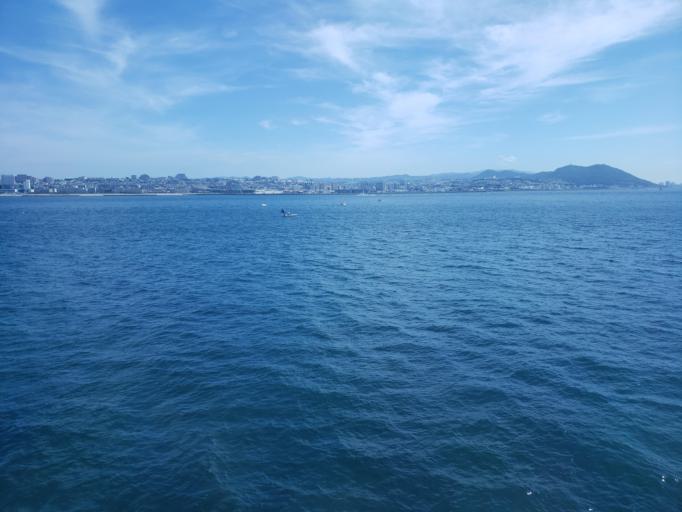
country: JP
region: Hyogo
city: Akashi
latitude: 34.6095
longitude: 135.0392
